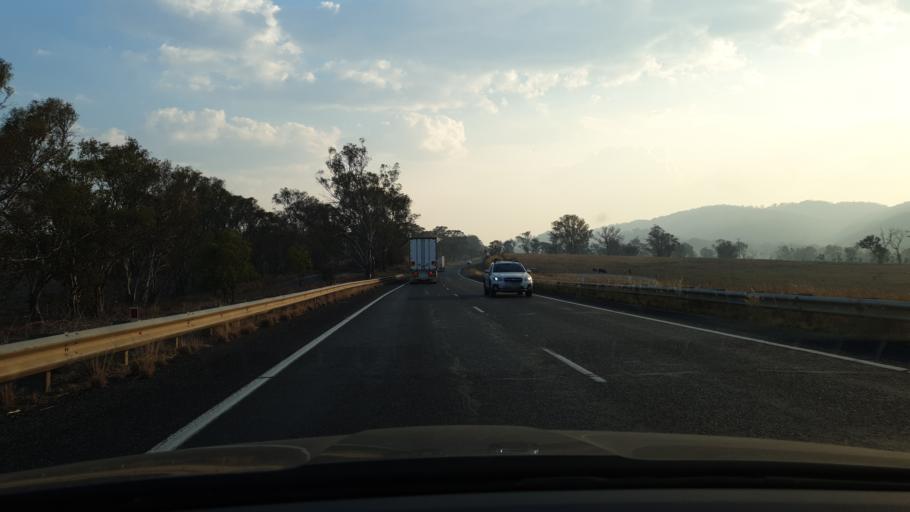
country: AU
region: New South Wales
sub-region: Tenterfield Municipality
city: Carrolls Creek
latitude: -29.1060
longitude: 152.0001
